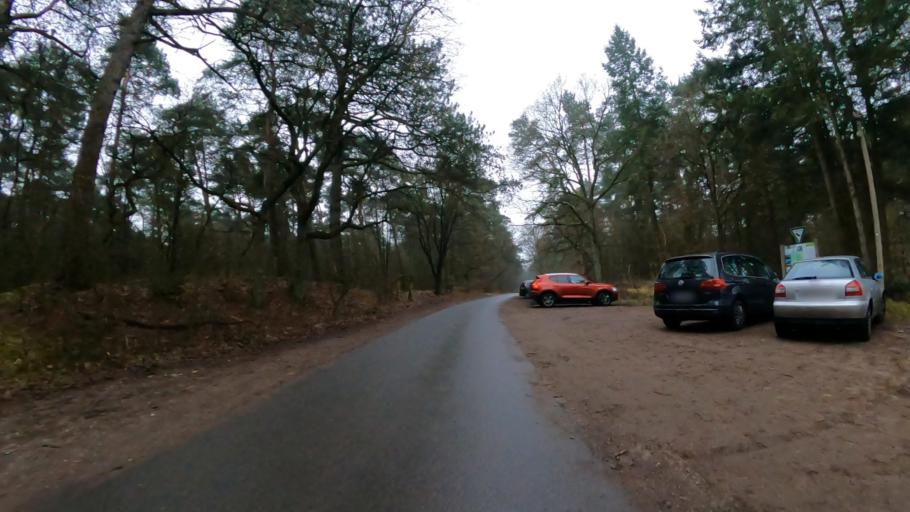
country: DE
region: Schleswig-Holstein
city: Appen
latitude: 53.6006
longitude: 9.7662
